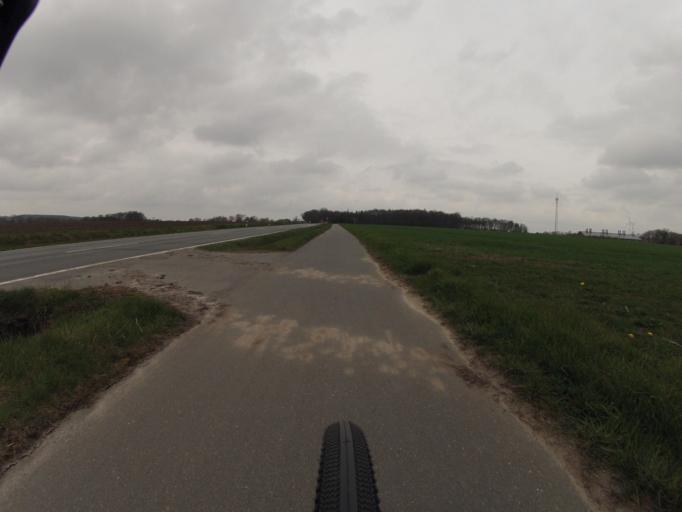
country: DE
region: North Rhine-Westphalia
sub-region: Regierungsbezirk Munster
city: Mettingen
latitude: 52.3327
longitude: 7.7478
